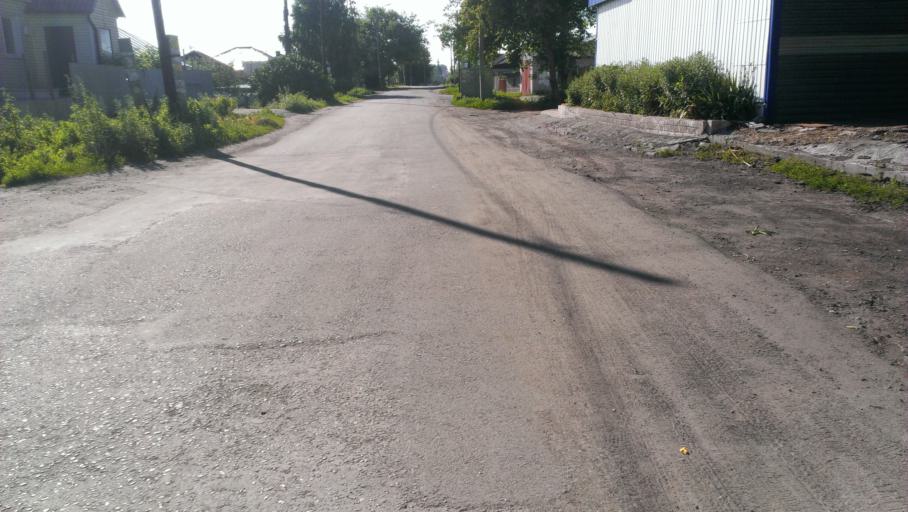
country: RU
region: Altai Krai
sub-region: Gorod Barnaulskiy
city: Barnaul
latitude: 53.3545
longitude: 83.7536
